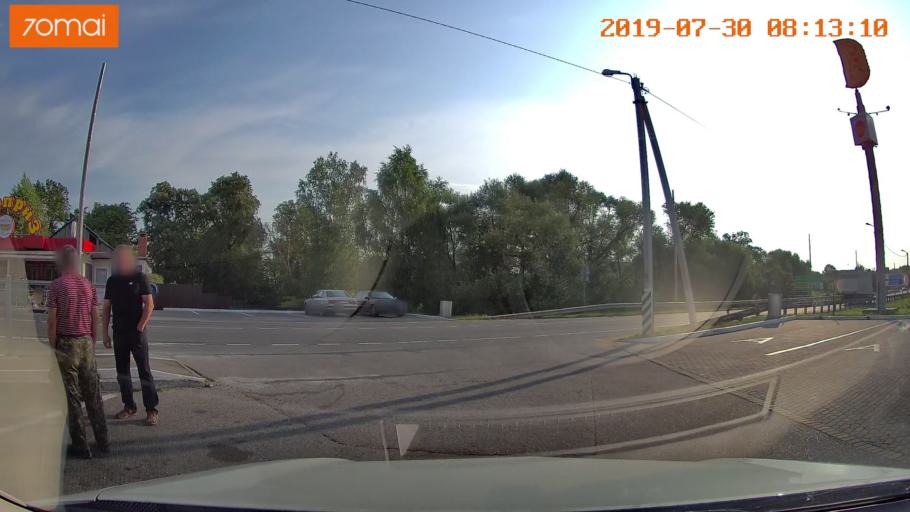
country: RU
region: Kaliningrad
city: Gvardeysk
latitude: 54.6504
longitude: 21.3429
